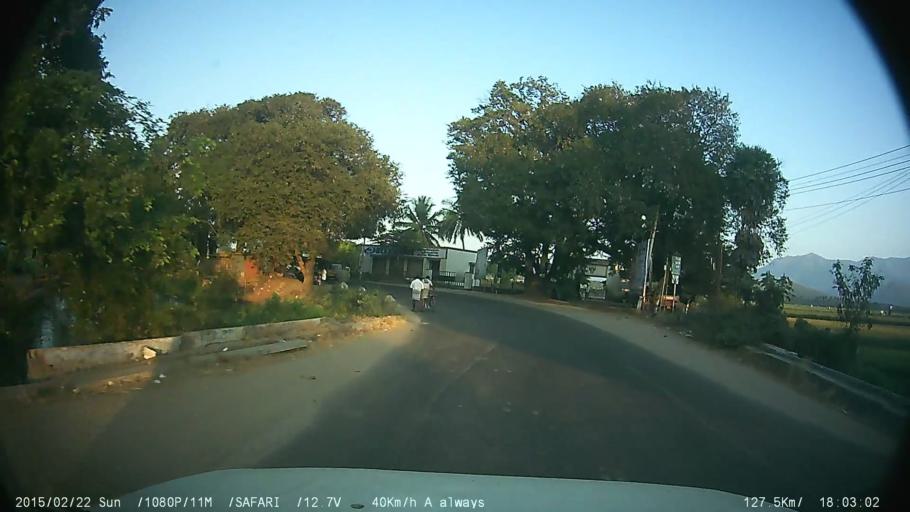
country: IN
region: Tamil Nadu
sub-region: Theni
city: Uttamapalaiyam
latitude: 9.8090
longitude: 77.3409
